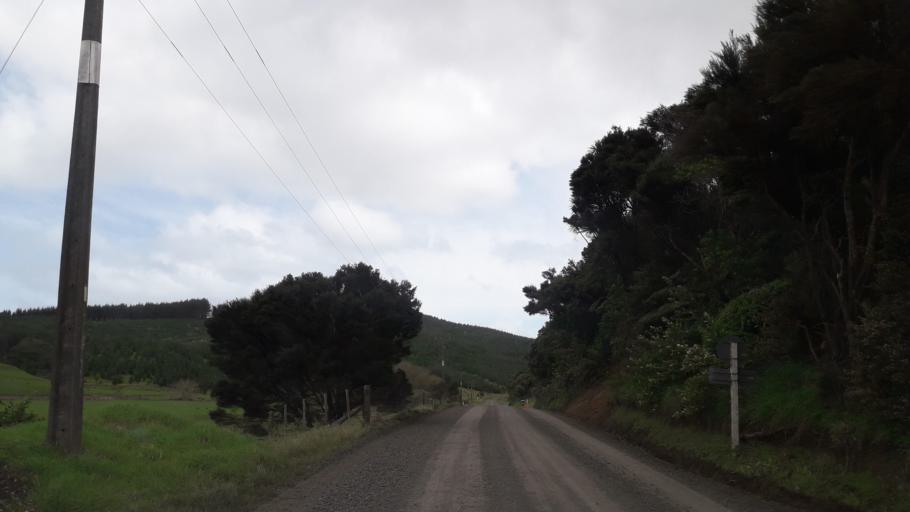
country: NZ
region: Northland
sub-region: Far North District
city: Ahipara
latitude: -35.4343
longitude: 173.3453
